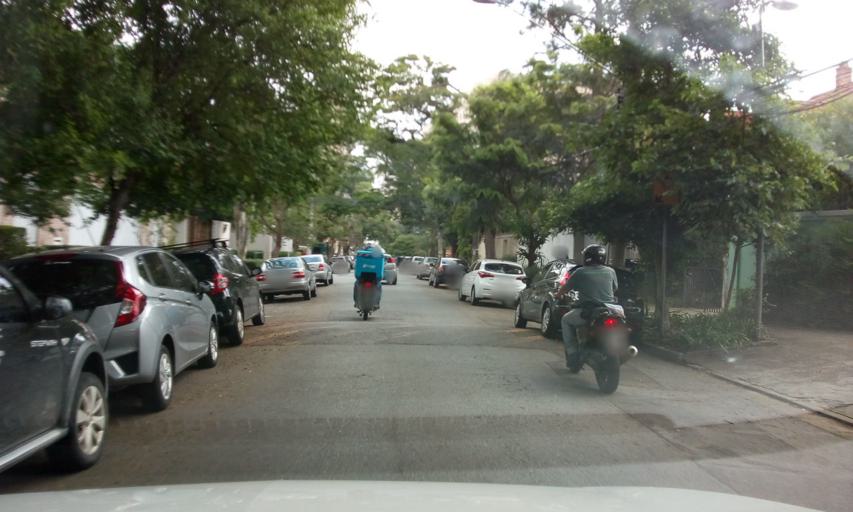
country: BR
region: Sao Paulo
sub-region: Sao Paulo
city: Sao Paulo
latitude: -23.5765
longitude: -46.6690
